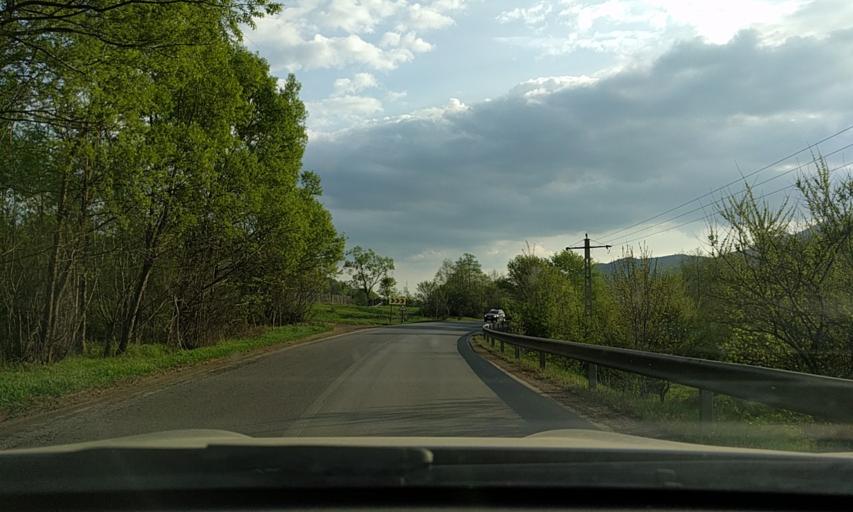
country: RO
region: Bacau
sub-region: Oras Slanic-Moldova
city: Slanic-Moldova
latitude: 46.1315
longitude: 26.4433
